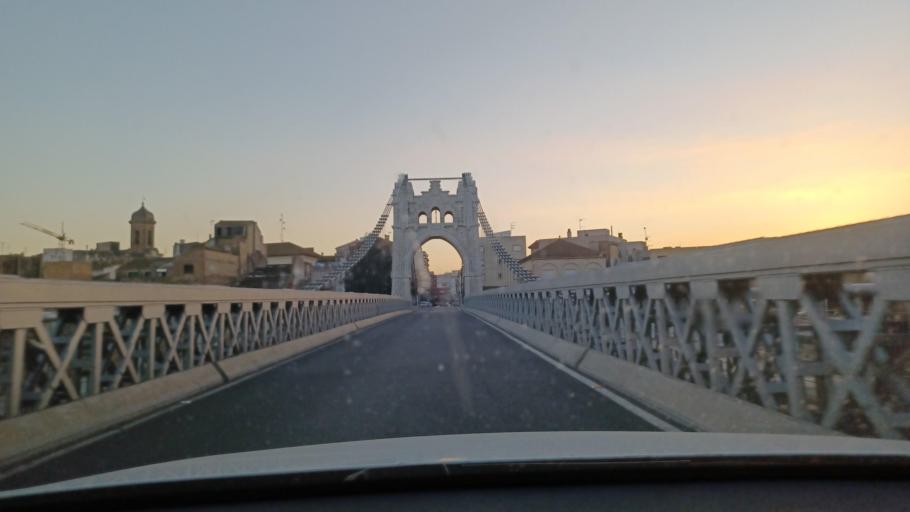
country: ES
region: Catalonia
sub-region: Provincia de Tarragona
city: Amposta
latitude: 40.7149
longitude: 0.5817
